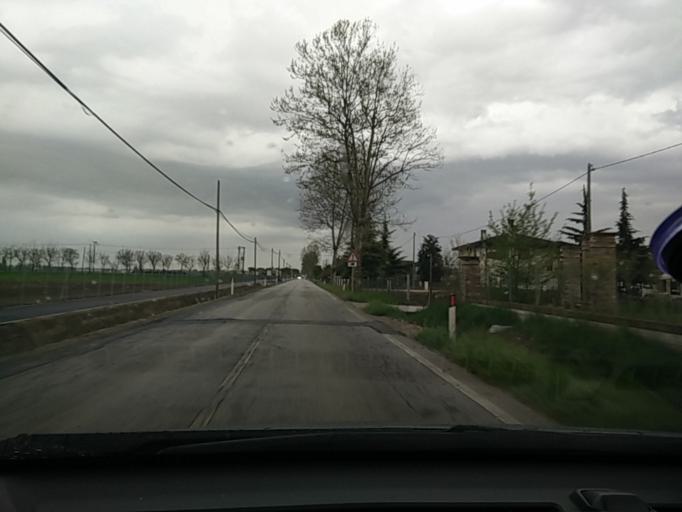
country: IT
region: Veneto
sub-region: Provincia di Treviso
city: Fornaci
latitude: 45.6485
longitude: 12.4648
